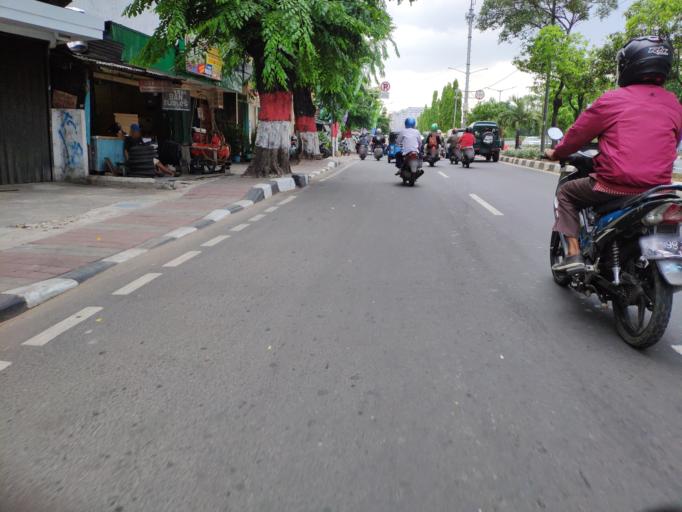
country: ID
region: Jakarta Raya
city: Jakarta
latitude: -6.1952
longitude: 106.8600
